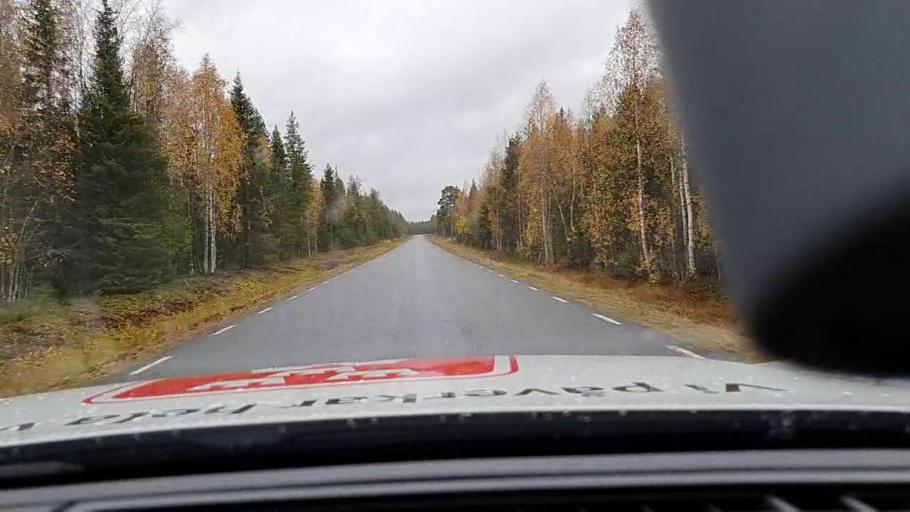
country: SE
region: Norrbotten
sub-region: Haparanda Kommun
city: Haparanda
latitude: 65.9348
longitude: 23.8126
